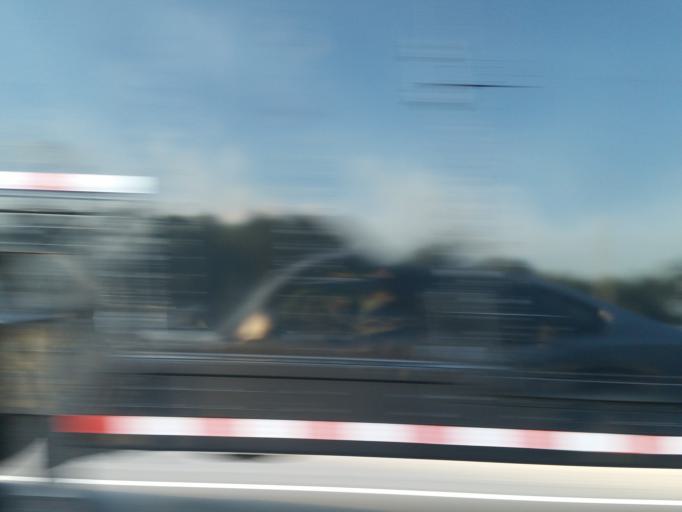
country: US
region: Florida
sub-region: Sarasota County
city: Plantation
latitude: 27.1128
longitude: -82.3224
